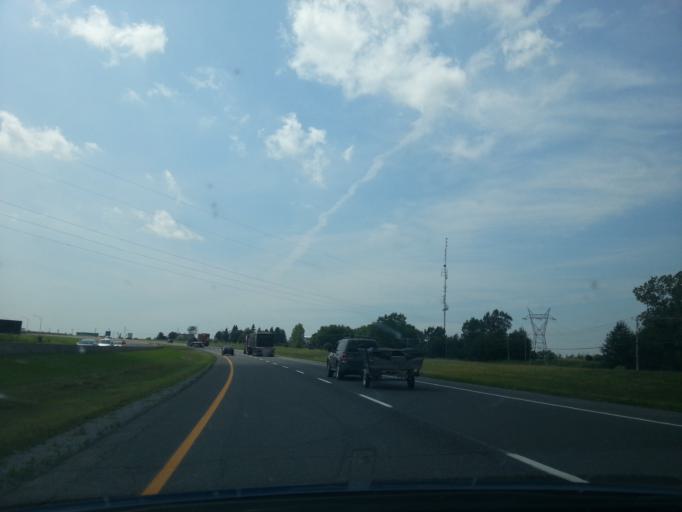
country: CA
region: Quebec
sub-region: Centre-du-Quebec
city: Drummondville
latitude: 45.9115
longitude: -72.5090
